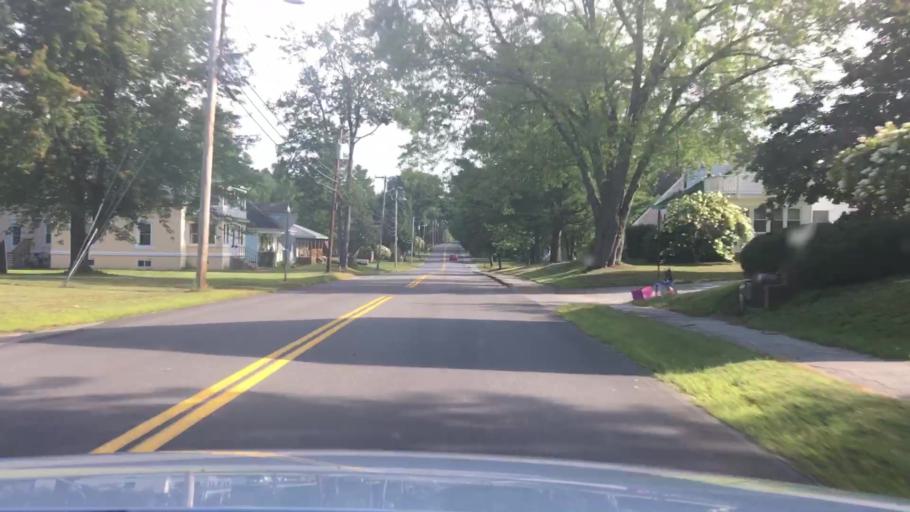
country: US
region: Maine
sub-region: Androscoggin County
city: Lisbon Falls
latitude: 44.0032
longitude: -70.0565
